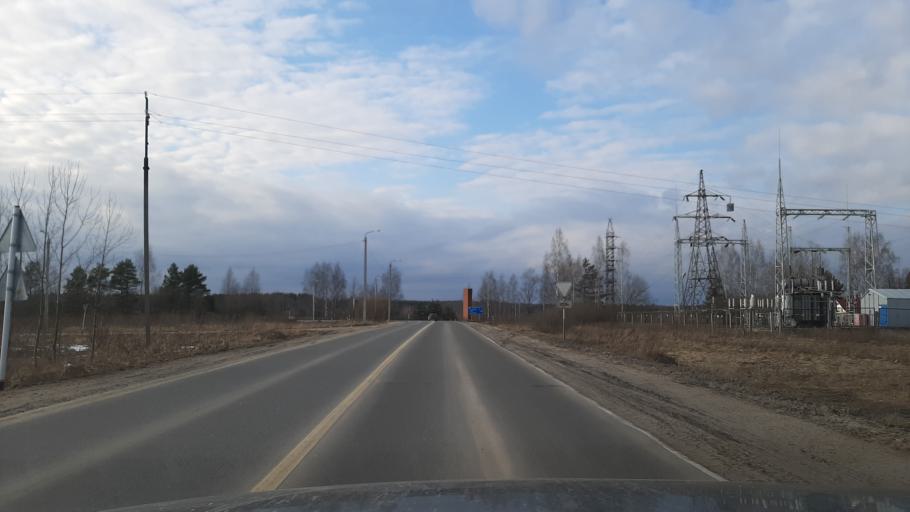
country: RU
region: Ivanovo
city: Novo-Talitsy
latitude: 56.9406
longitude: 40.7124
